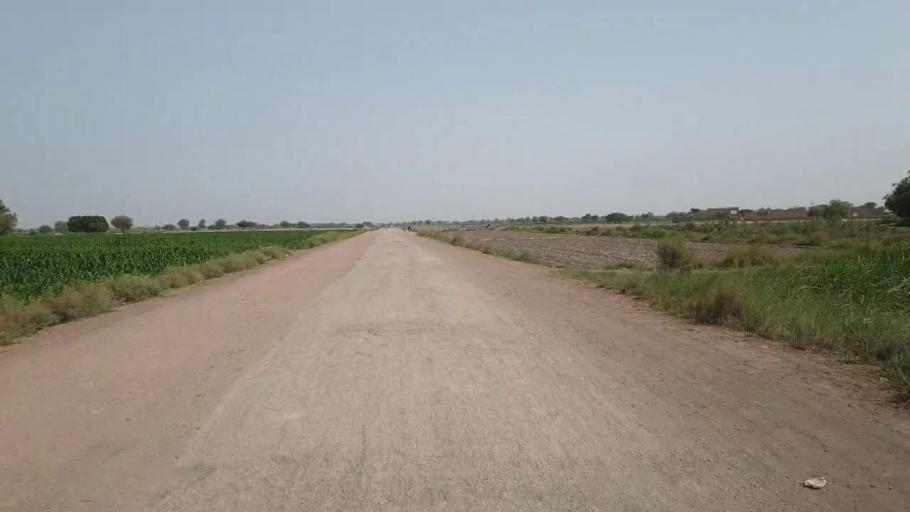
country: PK
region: Sindh
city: Daulatpur
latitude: 26.5534
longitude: 67.9909
